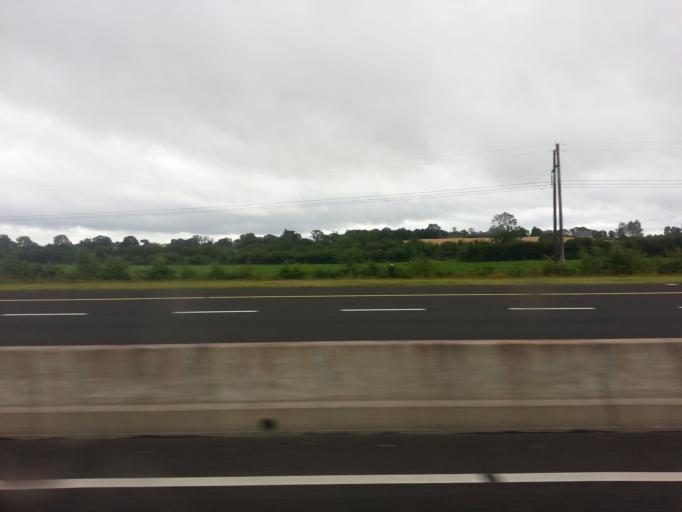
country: IE
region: Leinster
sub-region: Kilkenny
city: Kilkenny
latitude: 52.6349
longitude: -7.1540
